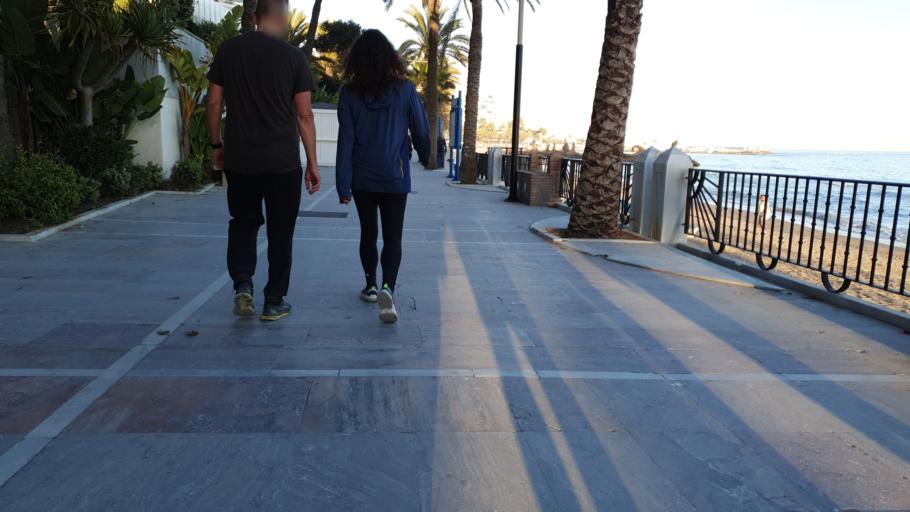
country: ES
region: Andalusia
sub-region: Provincia de Malaga
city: Marbella
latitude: 36.5067
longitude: -4.9000
